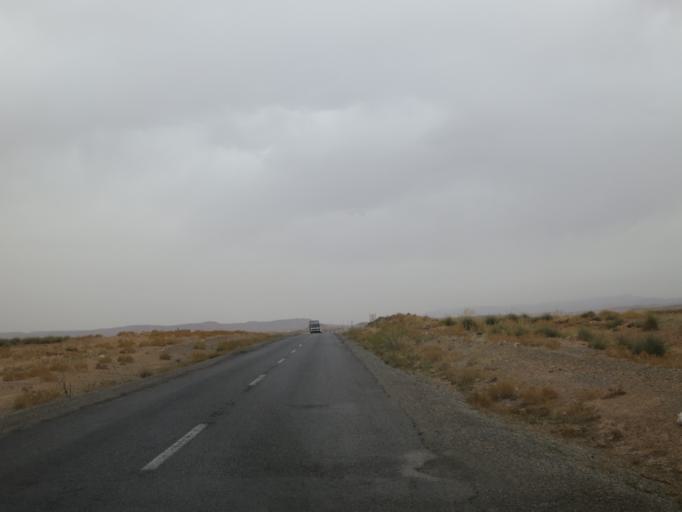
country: MA
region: Meknes-Tafilalet
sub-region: Khenifra
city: Midelt
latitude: 32.6975
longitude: -4.8278
